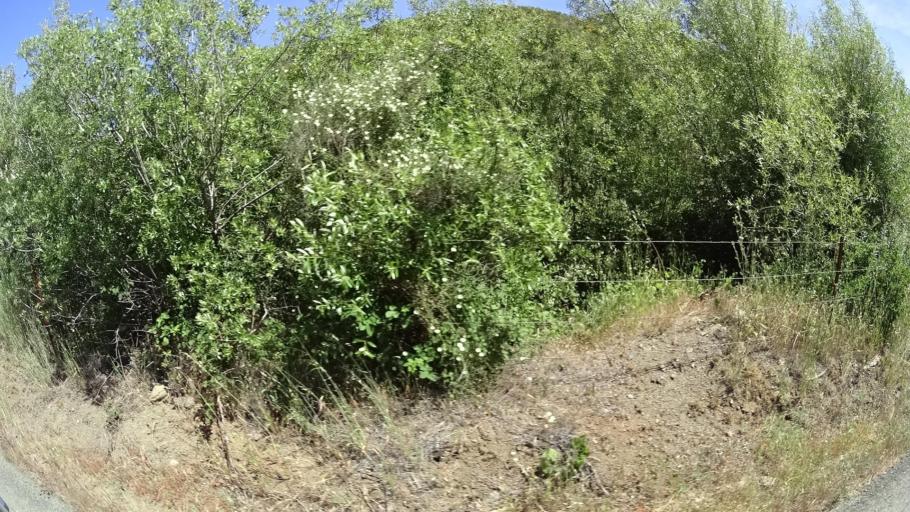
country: US
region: California
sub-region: Lake County
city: Middletown
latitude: 38.7812
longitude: -122.6461
